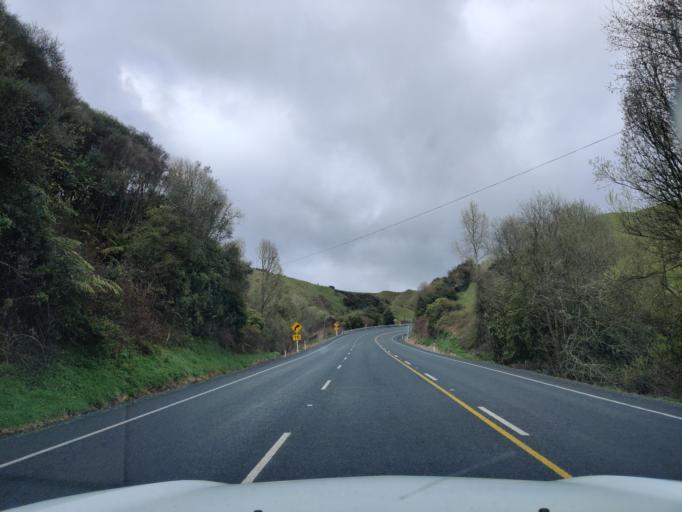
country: NZ
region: Waikato
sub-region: Otorohanga District
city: Otorohanga
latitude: -38.6327
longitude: 175.2091
